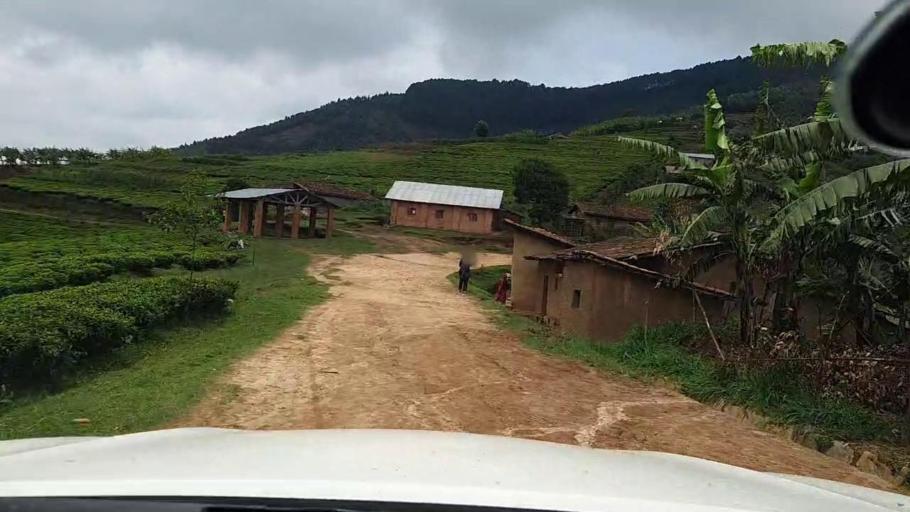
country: RW
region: Western Province
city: Kibuye
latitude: -2.1546
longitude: 29.4521
